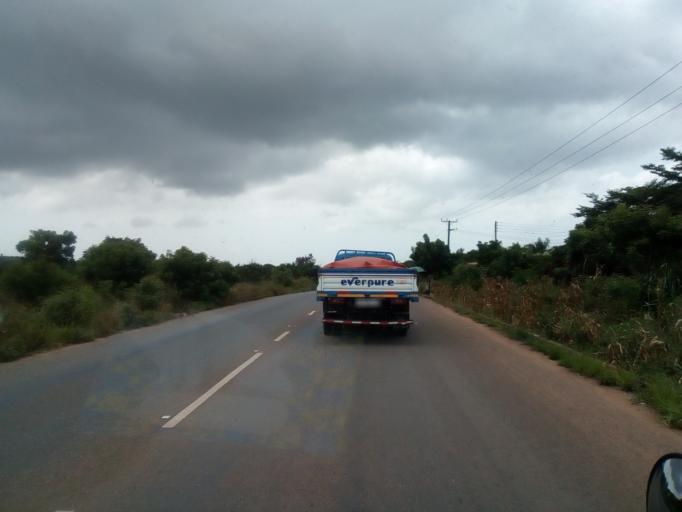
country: GH
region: Greater Accra
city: Dome
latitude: 5.6556
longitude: -0.2053
